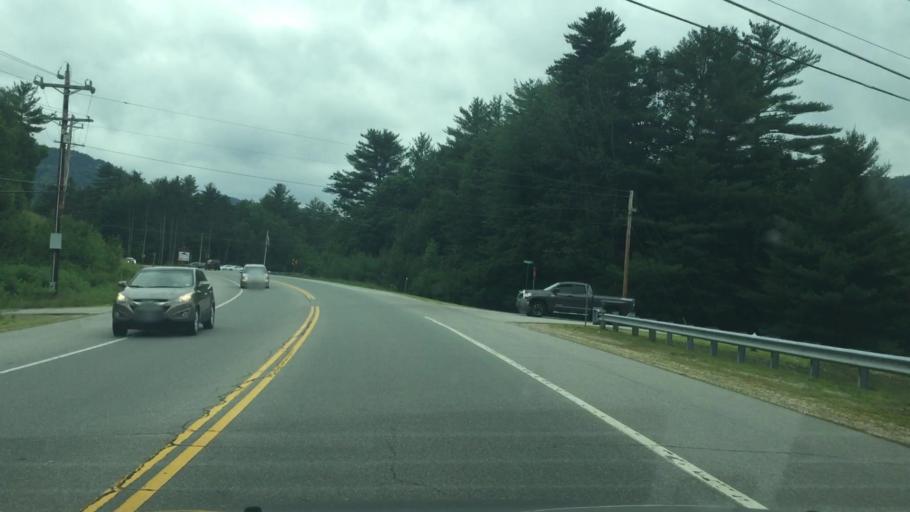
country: US
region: New Hampshire
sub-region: Carroll County
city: North Conway
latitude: 44.1027
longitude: -71.2007
